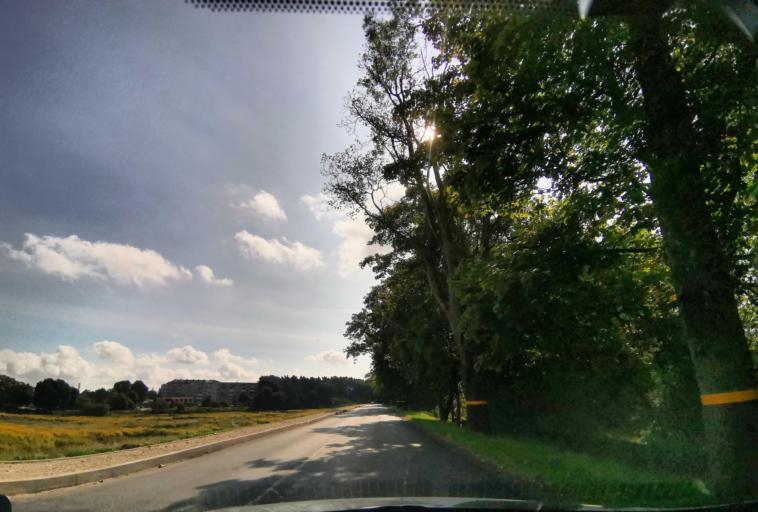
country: RU
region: Kaliningrad
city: Chernyakhovsk
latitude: 54.6536
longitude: 21.8132
